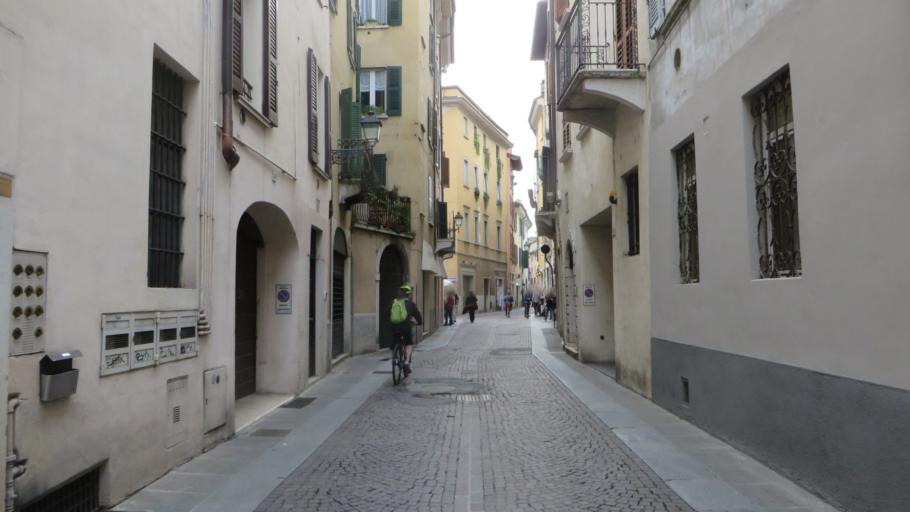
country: IT
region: Lombardy
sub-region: Provincia di Brescia
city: Brescia
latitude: 45.5383
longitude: 10.2257
